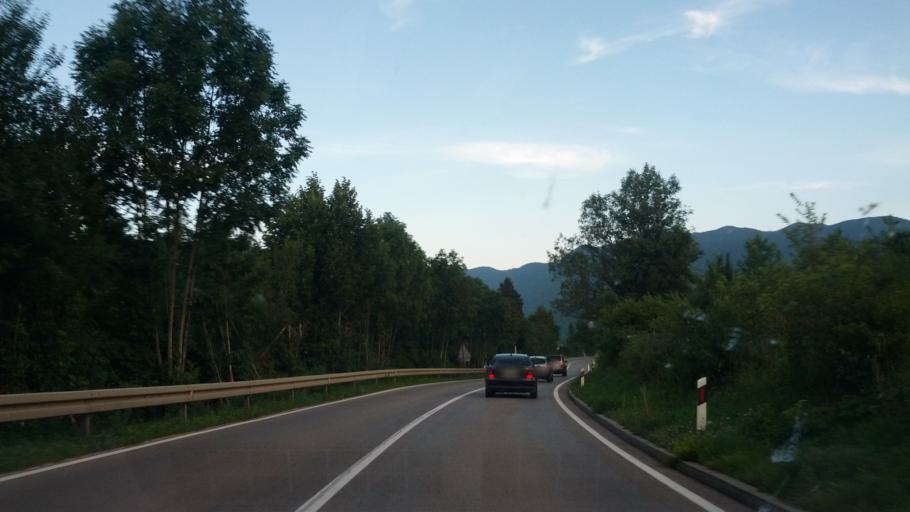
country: BA
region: Federation of Bosnia and Herzegovina
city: Izacic
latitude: 44.8869
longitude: 15.7266
